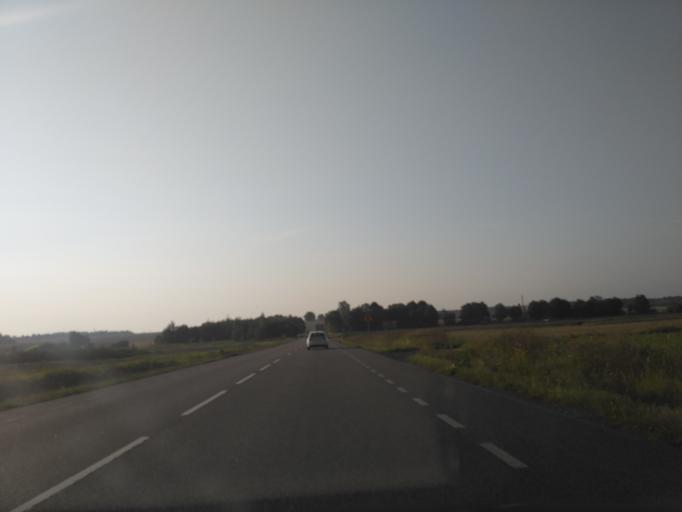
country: PL
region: Lublin Voivodeship
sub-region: Powiat janowski
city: Modliborzyce
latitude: 50.7355
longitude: 22.3537
